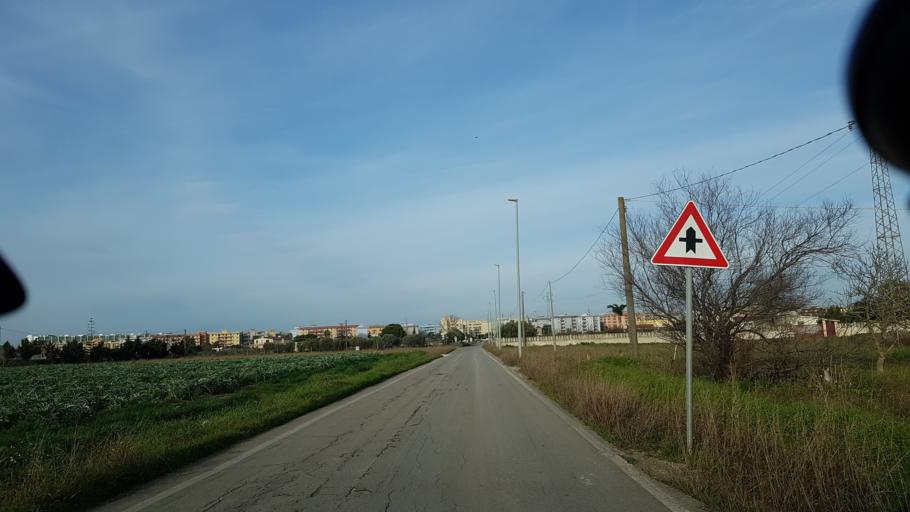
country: IT
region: Apulia
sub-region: Provincia di Brindisi
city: Brindisi
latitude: 40.6118
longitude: 17.9144
